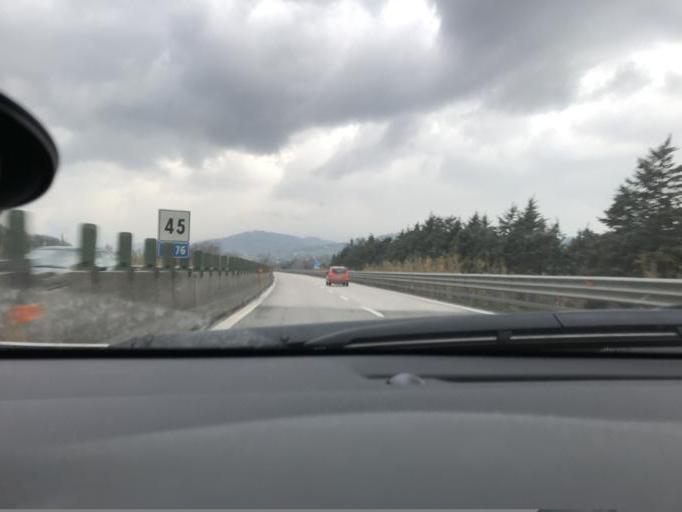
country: IT
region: The Marches
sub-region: Provincia di Ancona
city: Maiolati Spontini
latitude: 43.4947
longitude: 13.1144
